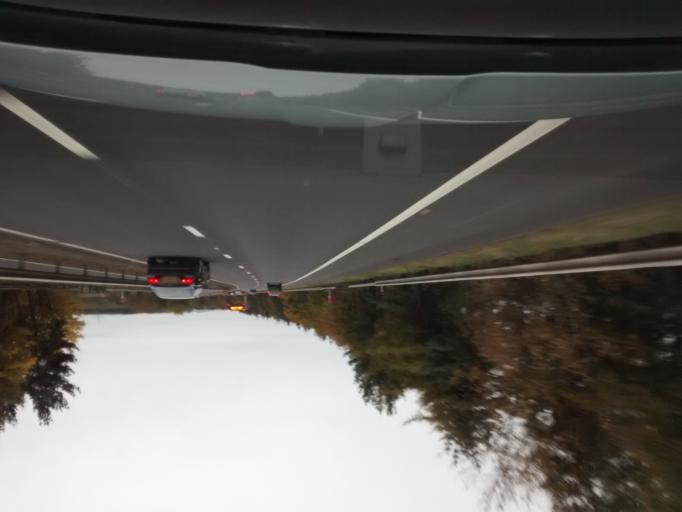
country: GB
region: Scotland
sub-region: Stirling
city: Cowie
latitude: 56.0533
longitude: -3.8400
